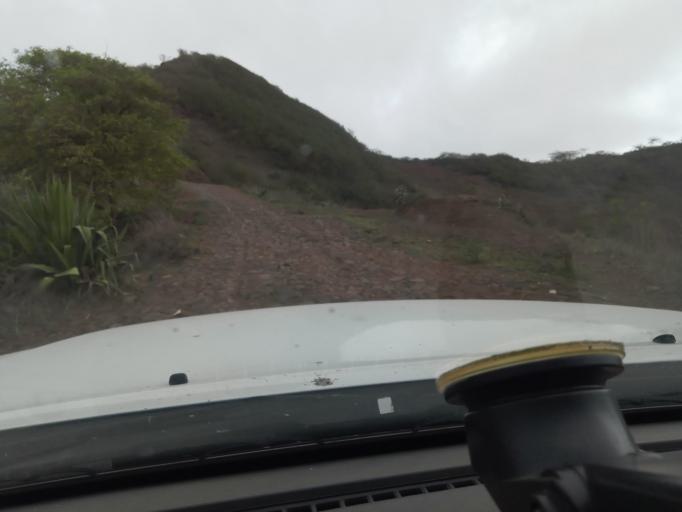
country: CV
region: Sao Salvador do Mundo
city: Picos
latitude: 15.1417
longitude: -23.6393
